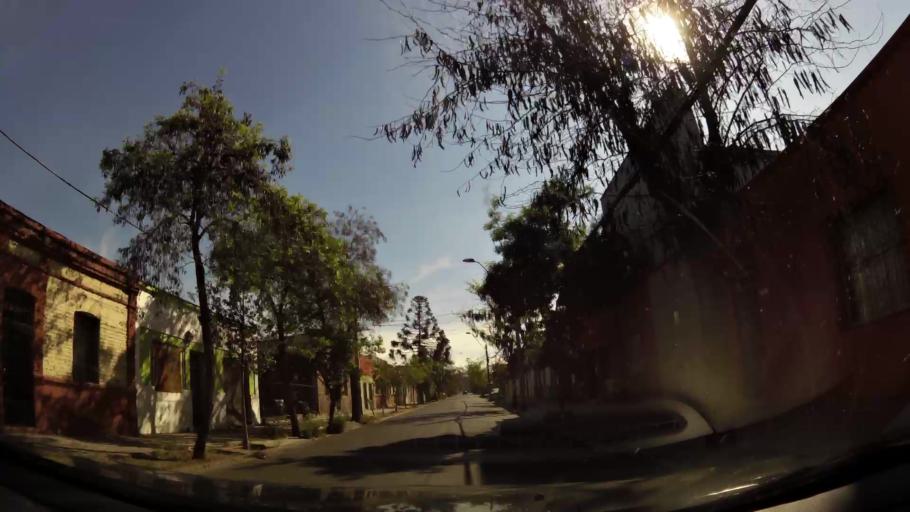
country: CL
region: Santiago Metropolitan
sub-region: Provincia de Santiago
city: Santiago
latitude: -33.4080
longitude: -70.6377
